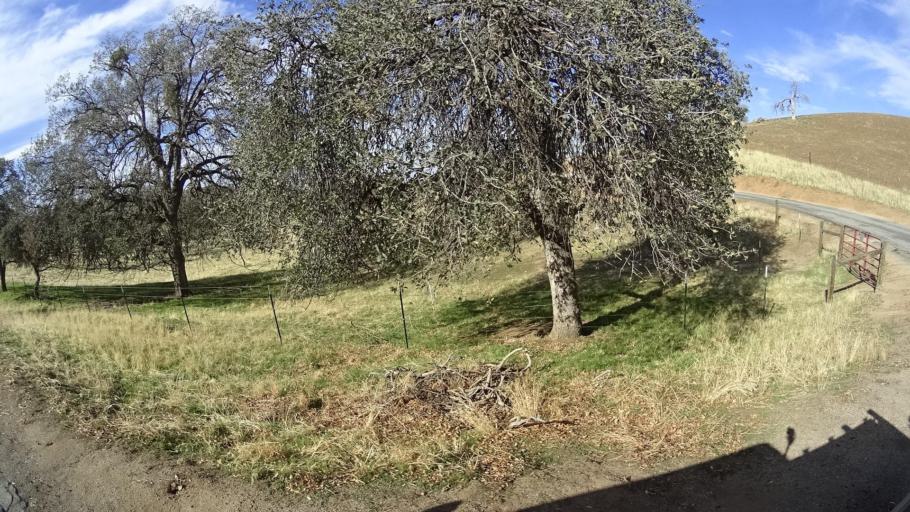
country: US
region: California
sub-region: Kern County
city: Oildale
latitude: 35.5881
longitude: -118.8257
